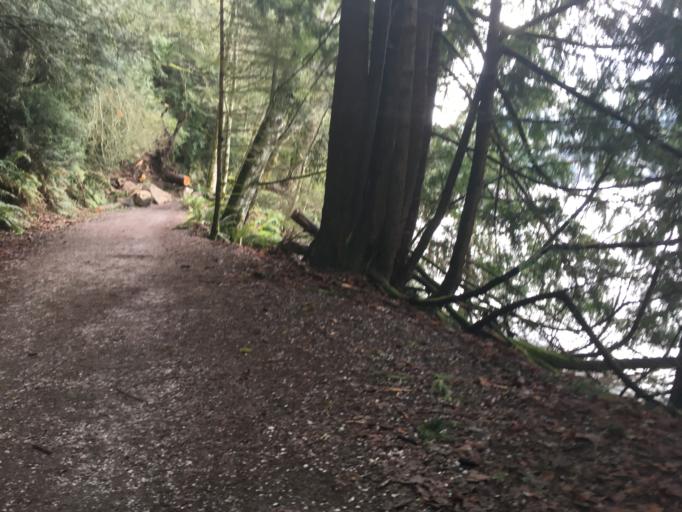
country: US
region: Washington
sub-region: Whatcom County
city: Sudden Valley
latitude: 48.7125
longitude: -122.2980
